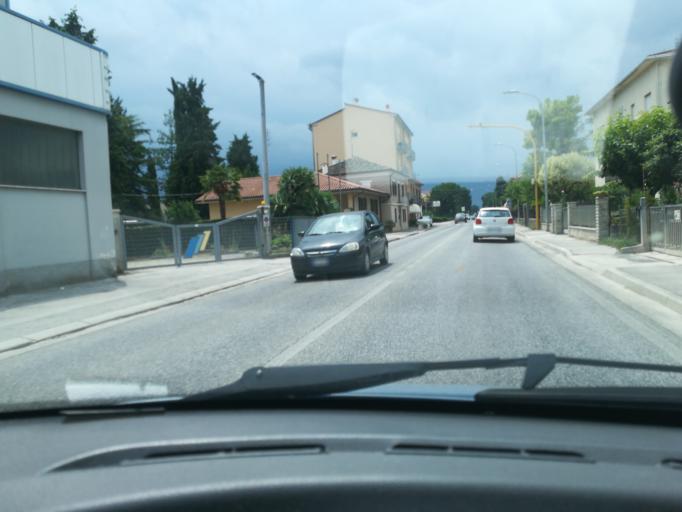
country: IT
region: The Marches
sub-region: Provincia di Macerata
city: Montecassiano
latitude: 43.3473
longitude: 13.4589
